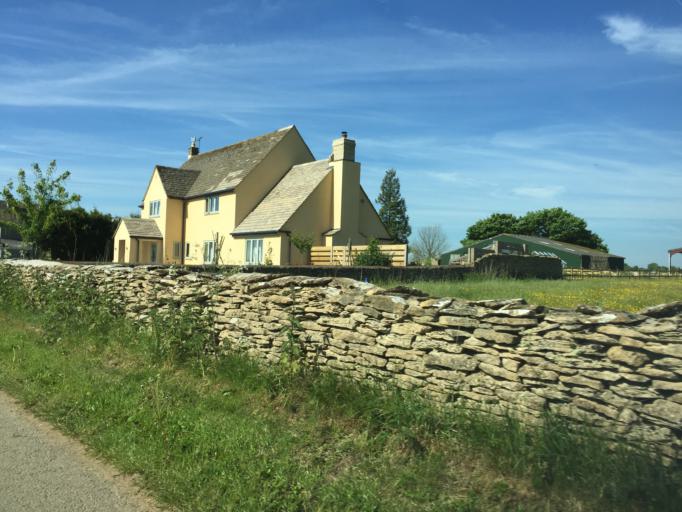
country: GB
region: England
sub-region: Wiltshire
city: Luckington
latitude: 51.6135
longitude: -2.2584
